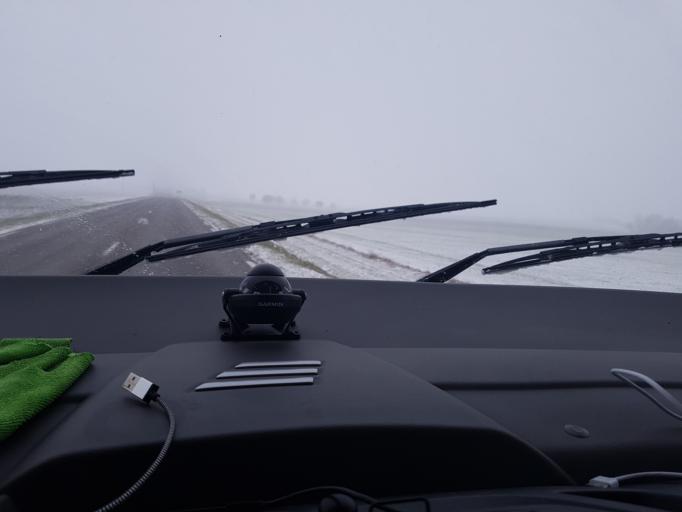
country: FR
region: Lorraine
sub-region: Departement de la Moselle
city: Chateau-Salins
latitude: 48.8715
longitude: 6.4203
